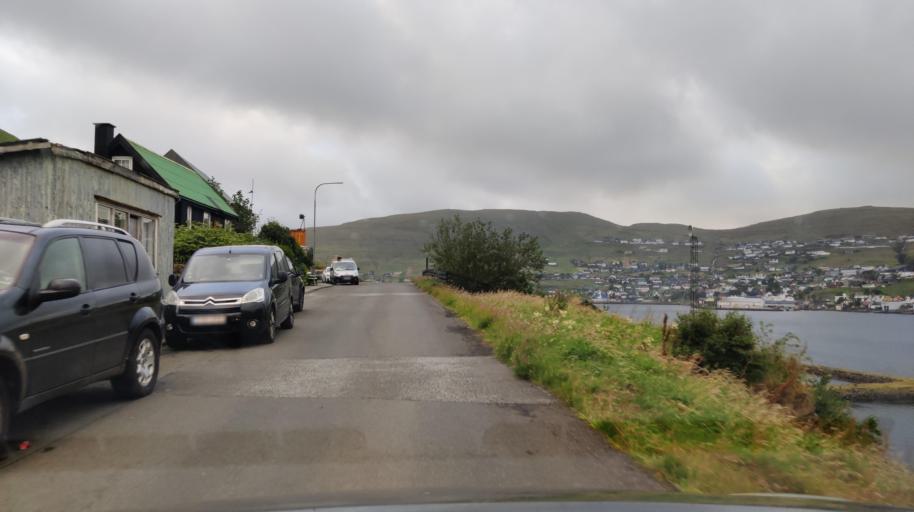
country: FO
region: Streymoy
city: Vestmanna
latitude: 62.1503
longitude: -7.1509
